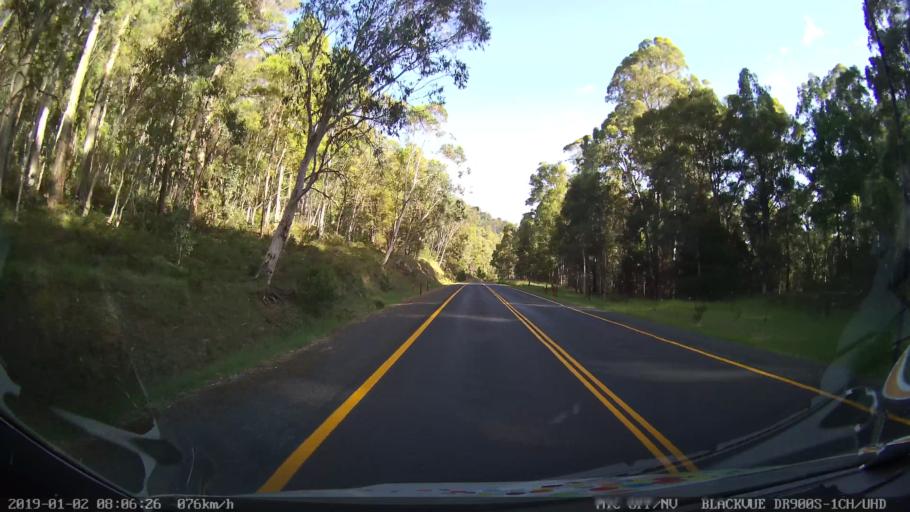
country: AU
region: New South Wales
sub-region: Tumut Shire
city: Tumut
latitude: -35.6401
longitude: 148.3870
